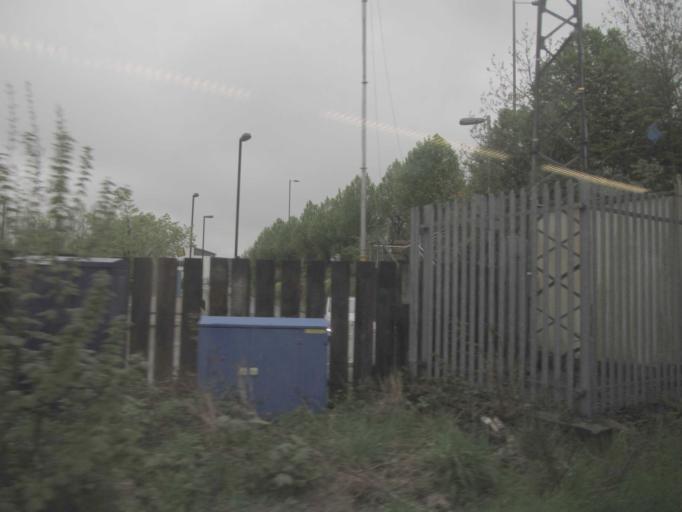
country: GB
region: England
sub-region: Bracknell Forest
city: Sandhurst
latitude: 51.3314
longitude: -0.7764
